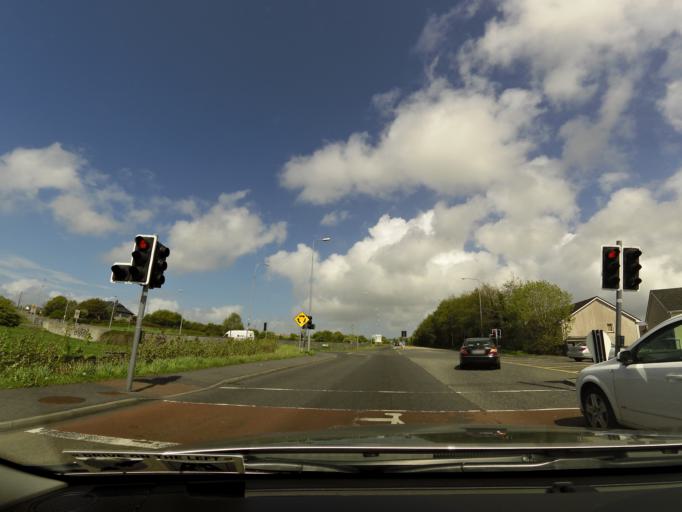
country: IE
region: Connaught
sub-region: County Galway
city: Oranmore
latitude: 53.2778
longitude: -8.9760
